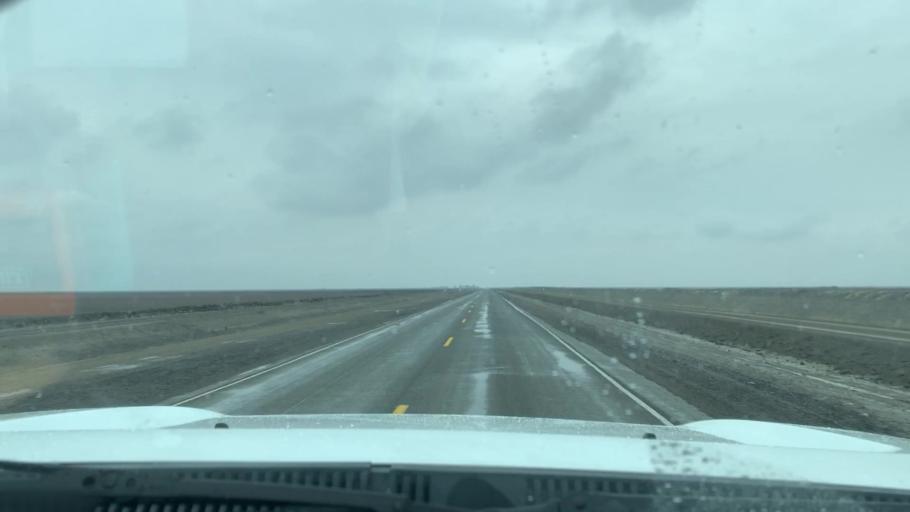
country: US
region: California
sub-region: Tulare County
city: Alpaugh
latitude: 35.9343
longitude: -119.6041
